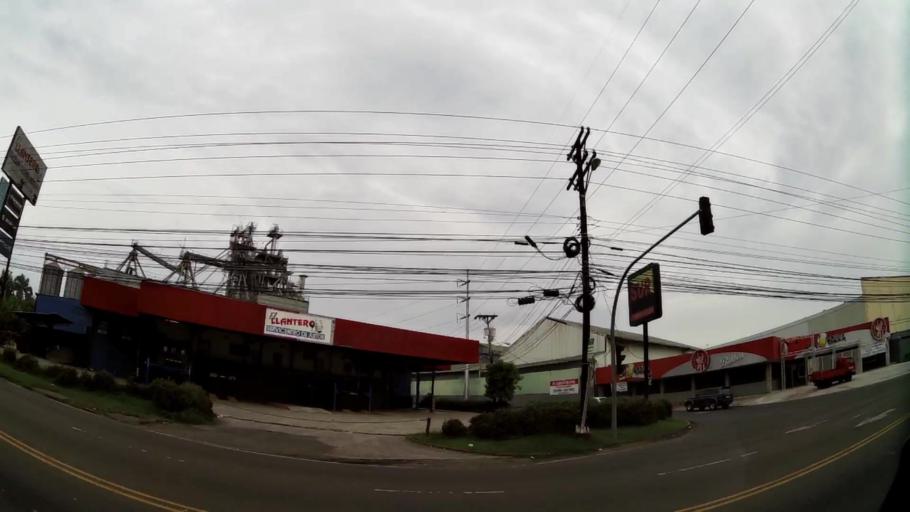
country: PA
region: Panama
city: San Miguelito
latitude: 9.0371
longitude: -79.4699
